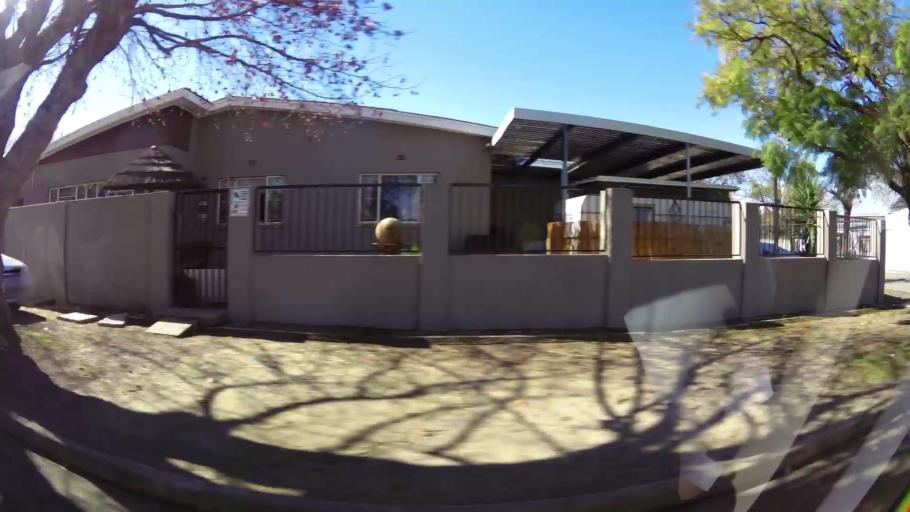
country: ZA
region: Western Cape
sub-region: Cape Winelands District Municipality
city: Ashton
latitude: -33.7979
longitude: 19.8853
